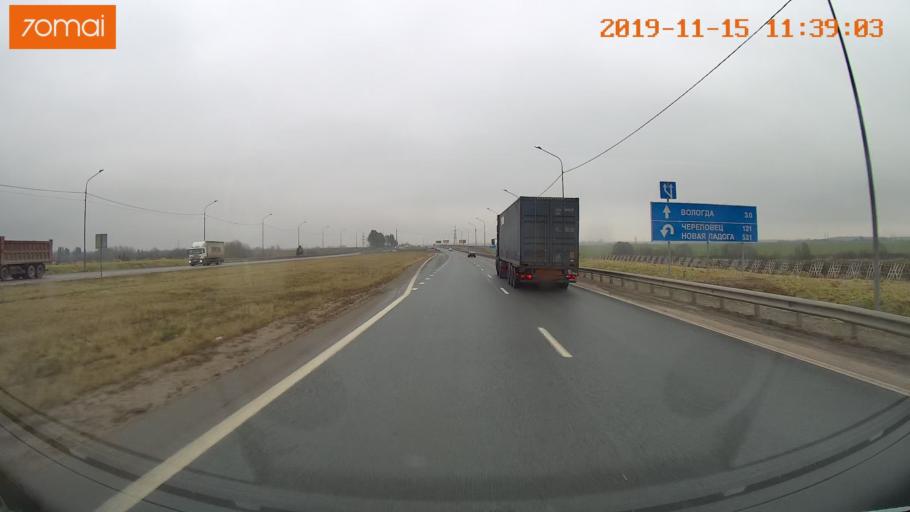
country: RU
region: Vologda
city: Molochnoye
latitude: 59.2109
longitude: 39.7137
